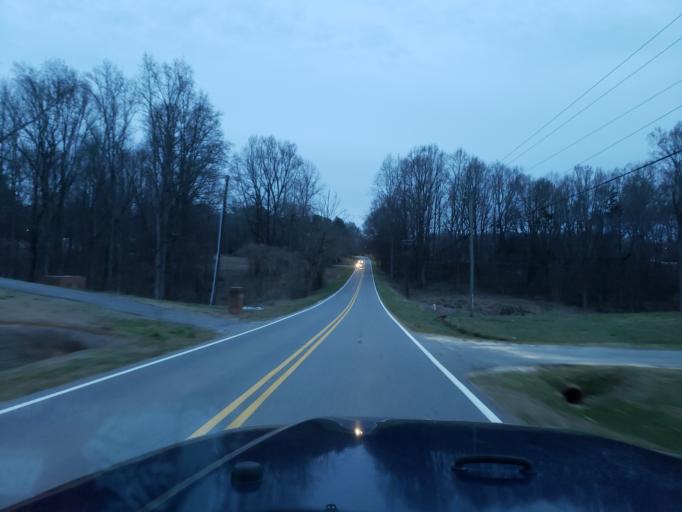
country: US
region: North Carolina
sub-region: Cleveland County
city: White Plains
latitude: 35.2445
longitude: -81.4597
